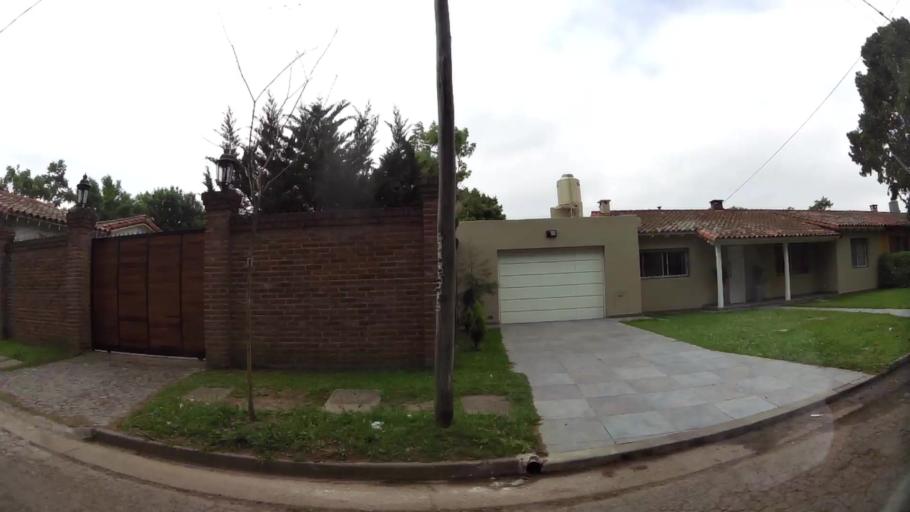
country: AR
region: Buenos Aires
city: San Justo
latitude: -34.7326
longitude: -58.5277
